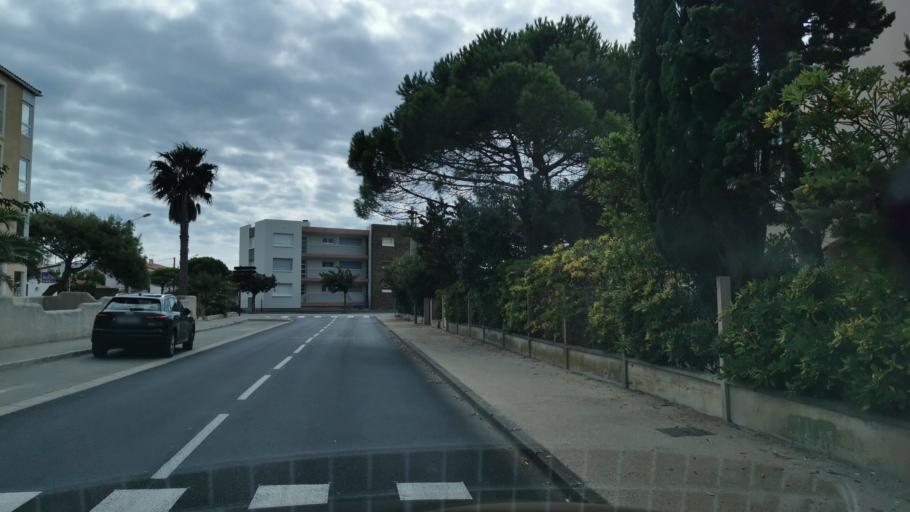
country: FR
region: Languedoc-Roussillon
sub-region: Departement de l'Aude
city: Fleury
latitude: 43.1625
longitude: 3.1676
